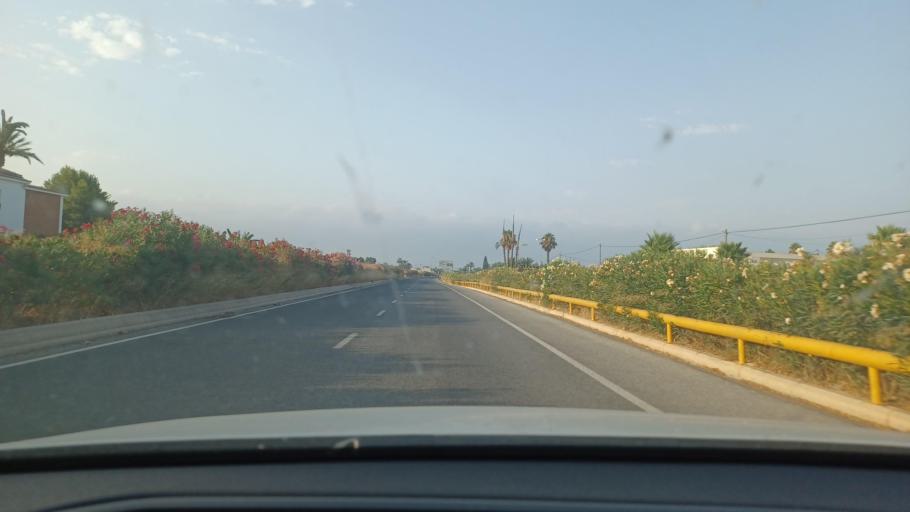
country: ES
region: Valencia
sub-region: Provincia de Alicante
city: Elche
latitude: 38.1924
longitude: -0.7011
